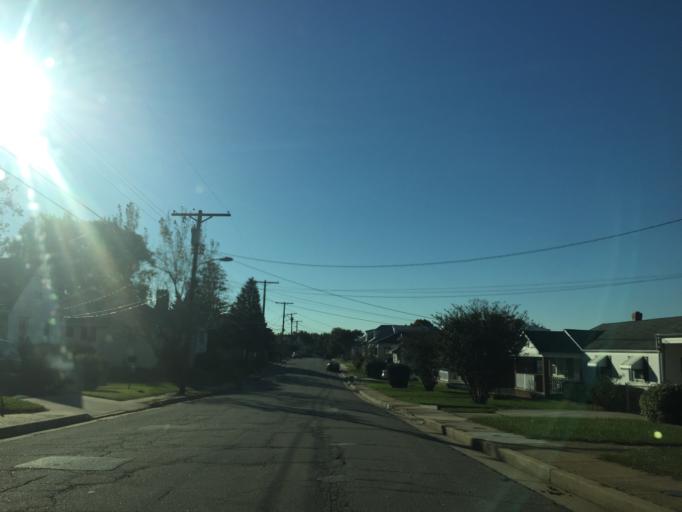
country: US
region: Maryland
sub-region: Baltimore County
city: Rosedale
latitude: 39.2878
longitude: -76.5261
